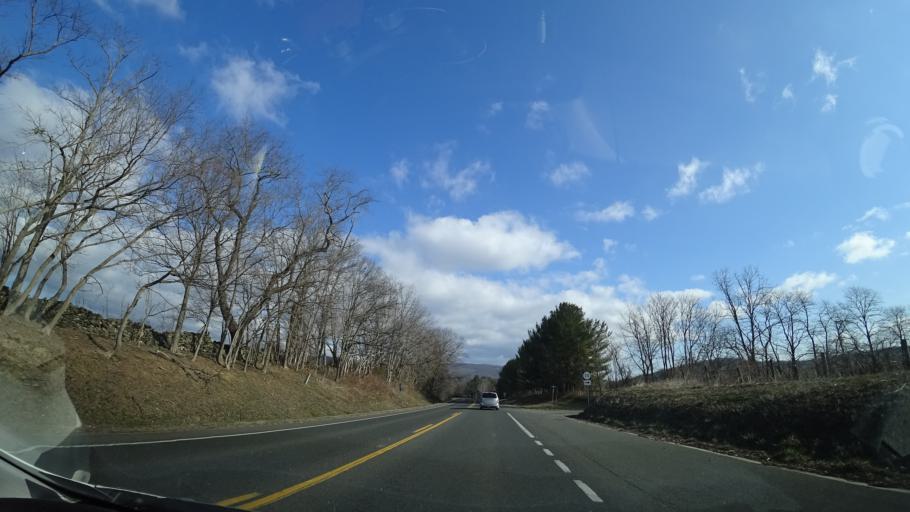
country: US
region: Virginia
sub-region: Warren County
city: Shenandoah Farms
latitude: 38.9816
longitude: -77.9499
